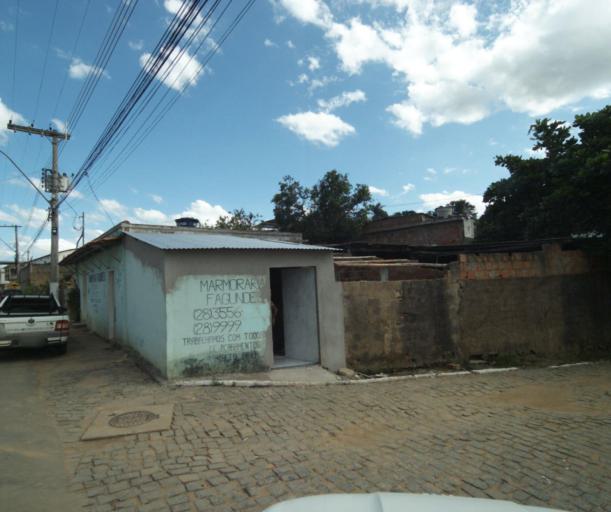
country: BR
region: Espirito Santo
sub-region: Sao Jose Do Calcado
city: Sao Jose do Calcado
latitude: -21.0390
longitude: -41.6526
